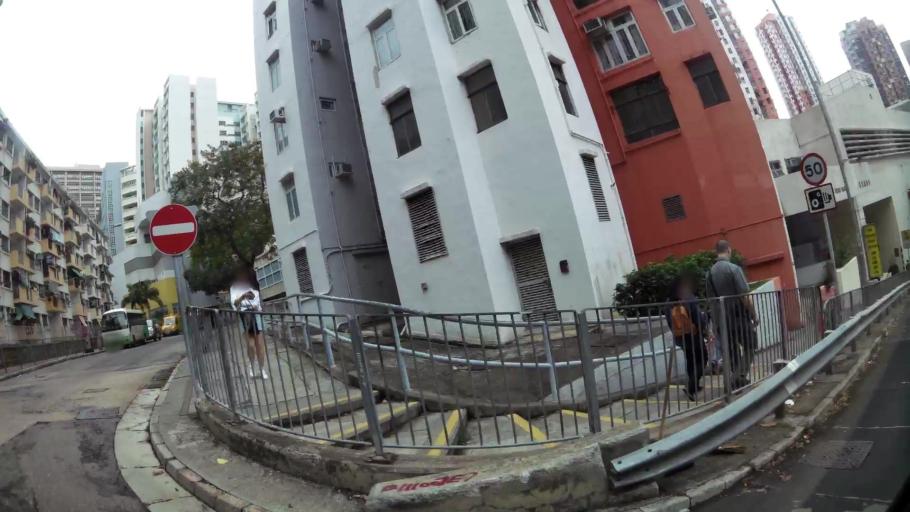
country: HK
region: Central and Western
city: Central
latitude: 22.2508
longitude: 114.1565
